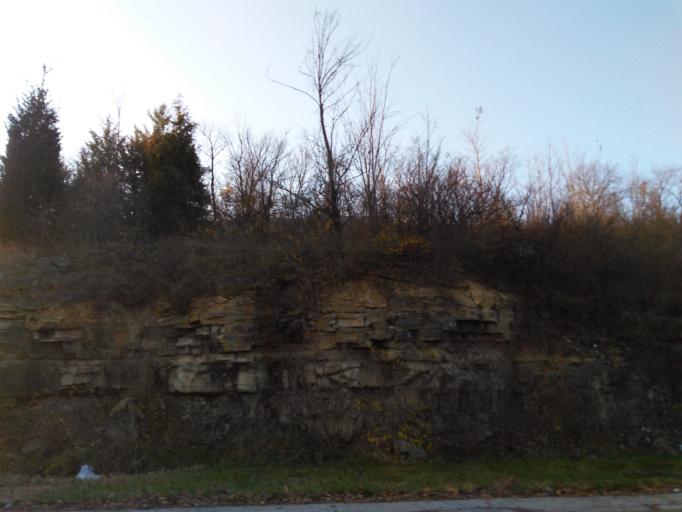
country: US
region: Missouri
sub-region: Saint Louis County
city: Concord
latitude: 38.5121
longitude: -90.3684
